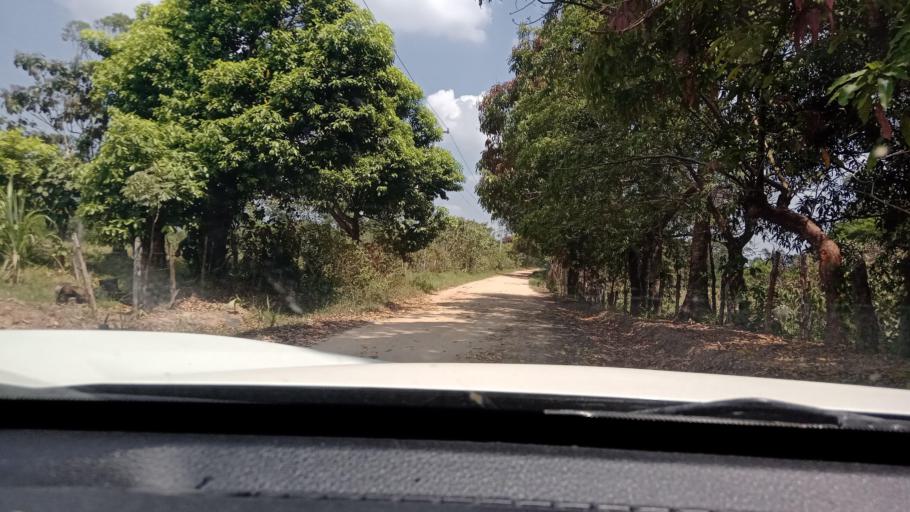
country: MX
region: Veracruz
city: Las Choapas
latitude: 17.9436
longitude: -94.1242
